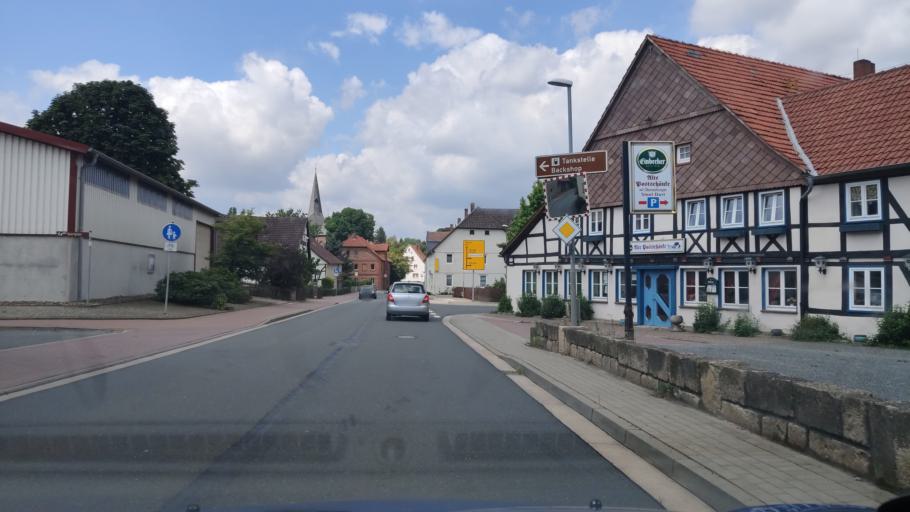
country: DE
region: Lower Saxony
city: Halle
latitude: 51.9899
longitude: 9.5661
